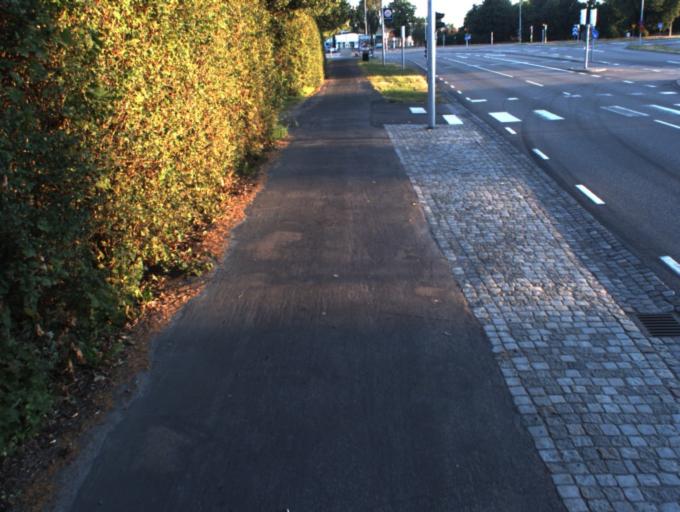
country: SE
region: Skane
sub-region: Helsingborg
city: Helsingborg
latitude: 56.0211
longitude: 12.7259
